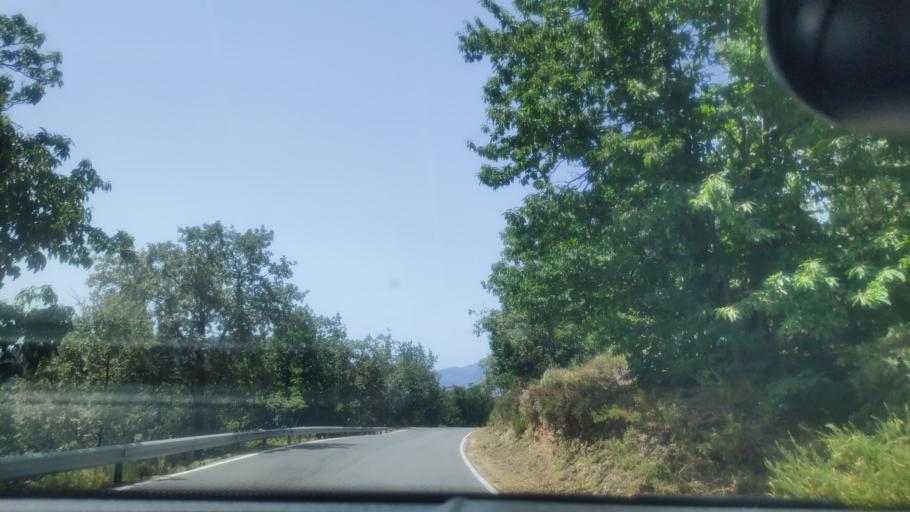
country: ES
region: Andalusia
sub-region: Provincia de Granada
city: Busquistar
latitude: 36.9550
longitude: -3.2785
